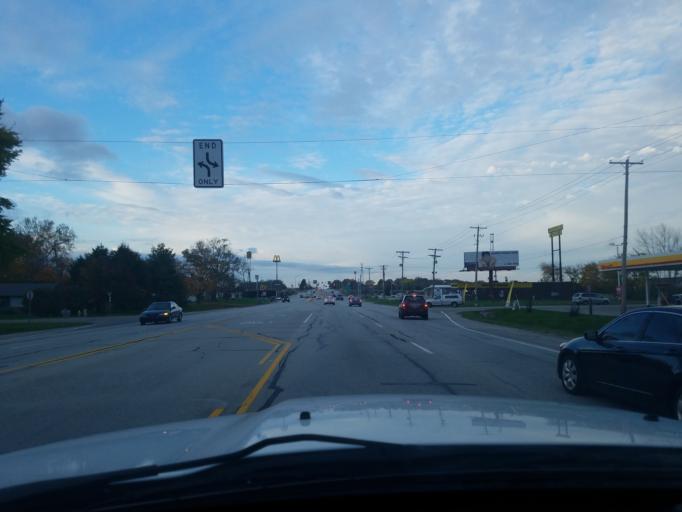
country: US
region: Indiana
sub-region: Shelby County
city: Shelbyville
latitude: 39.5455
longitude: -85.7755
